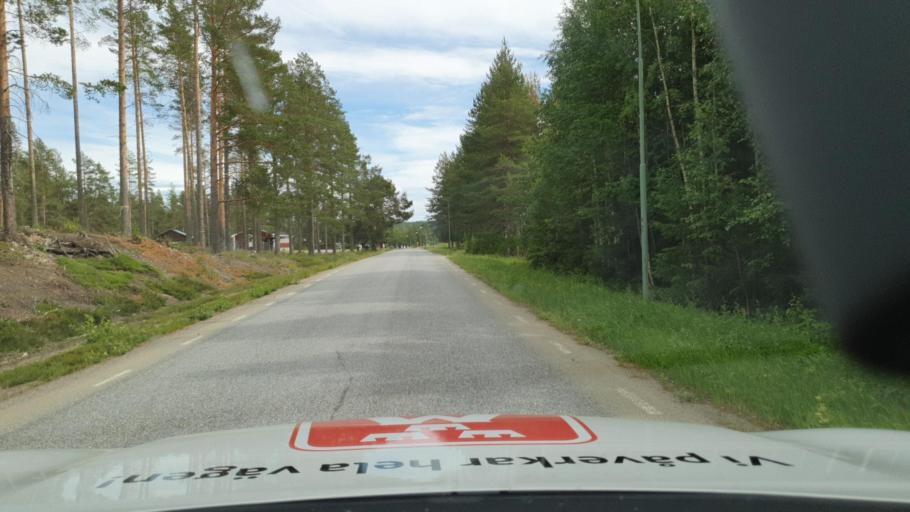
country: SE
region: Vaesterbotten
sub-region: Skelleftea Kommun
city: Burtraesk
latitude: 64.4997
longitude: 20.8505
